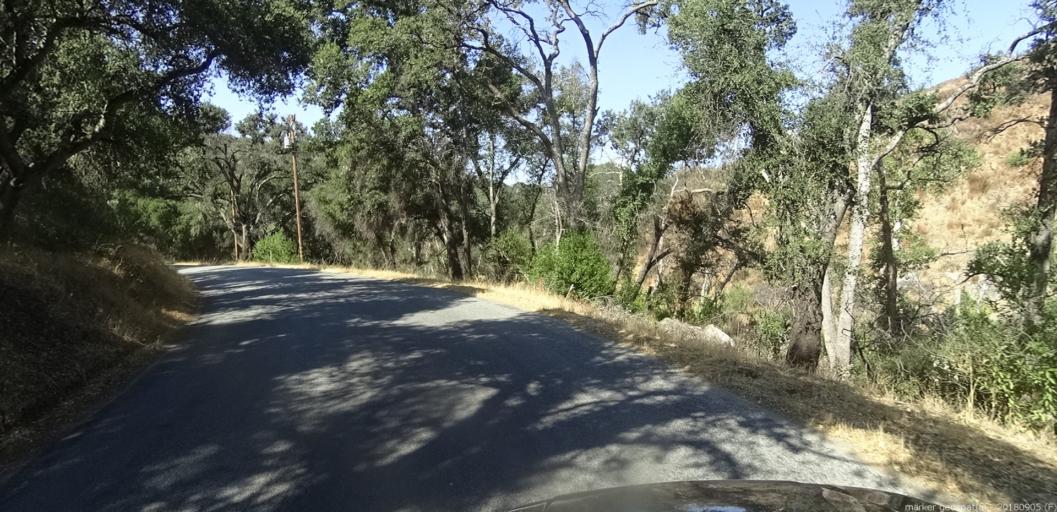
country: US
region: California
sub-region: Monterey County
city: Gonzales
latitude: 36.3923
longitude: -121.6010
